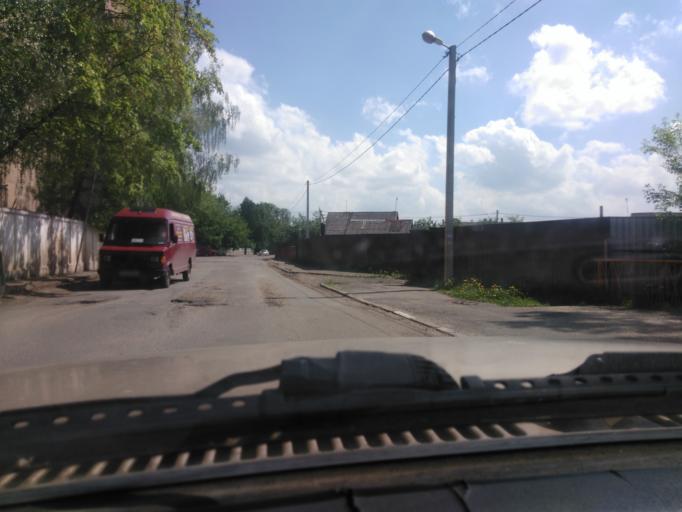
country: BY
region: Mogilev
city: Mahilyow
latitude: 53.9259
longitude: 30.3339
